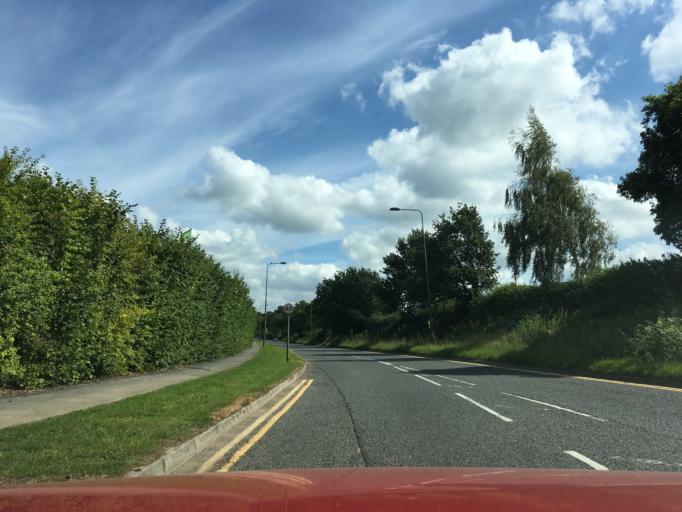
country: GB
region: England
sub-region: South Gloucestershire
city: Thornbury
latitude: 51.6015
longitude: -2.5156
